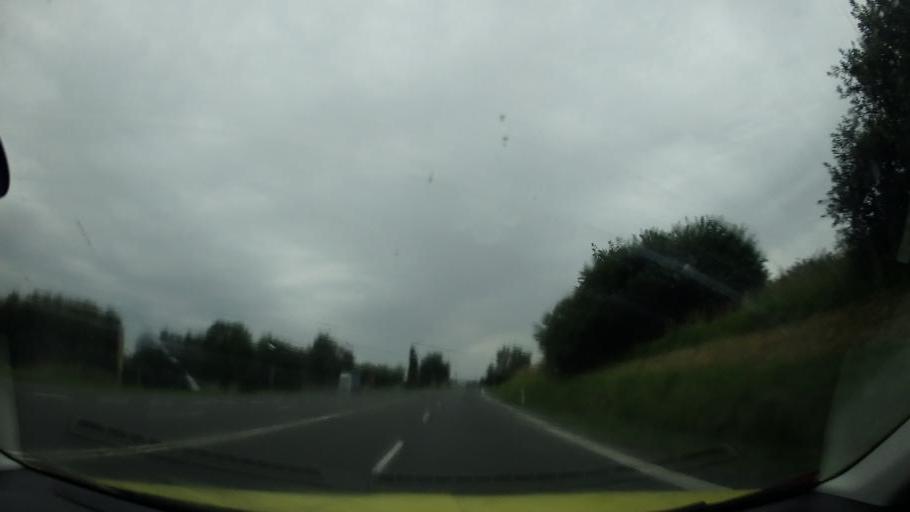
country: CZ
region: Olomoucky
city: Belotin
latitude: 49.5746
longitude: 17.7764
